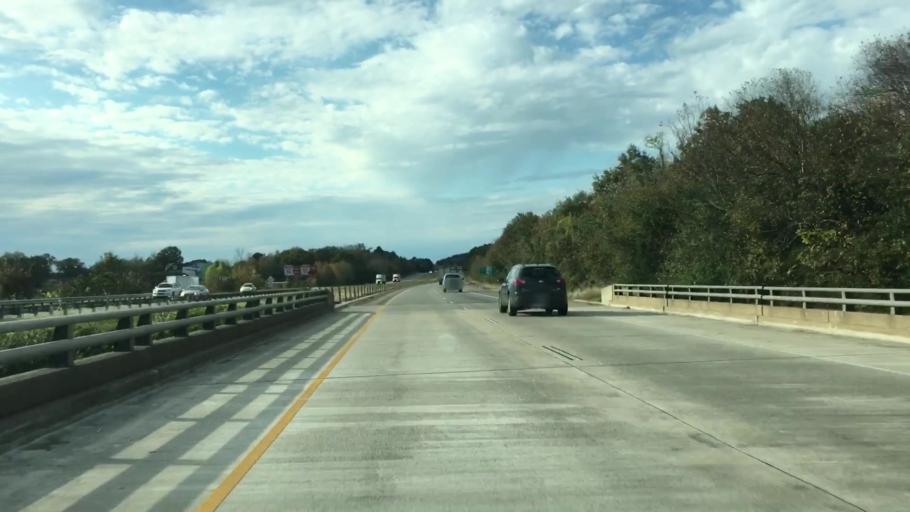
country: US
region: Arkansas
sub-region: Pope County
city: Pottsville
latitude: 35.2516
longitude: -93.0400
